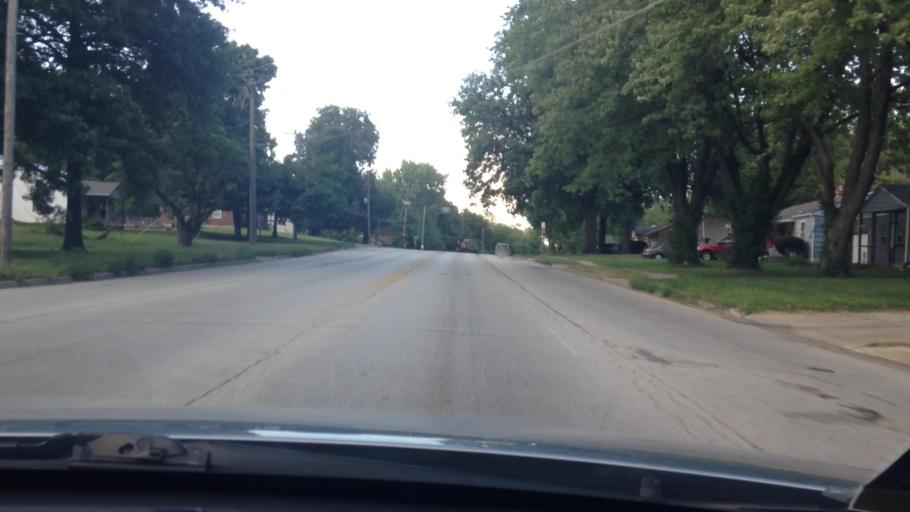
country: US
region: Missouri
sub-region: Jackson County
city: Raytown
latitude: 38.9892
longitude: -94.4828
